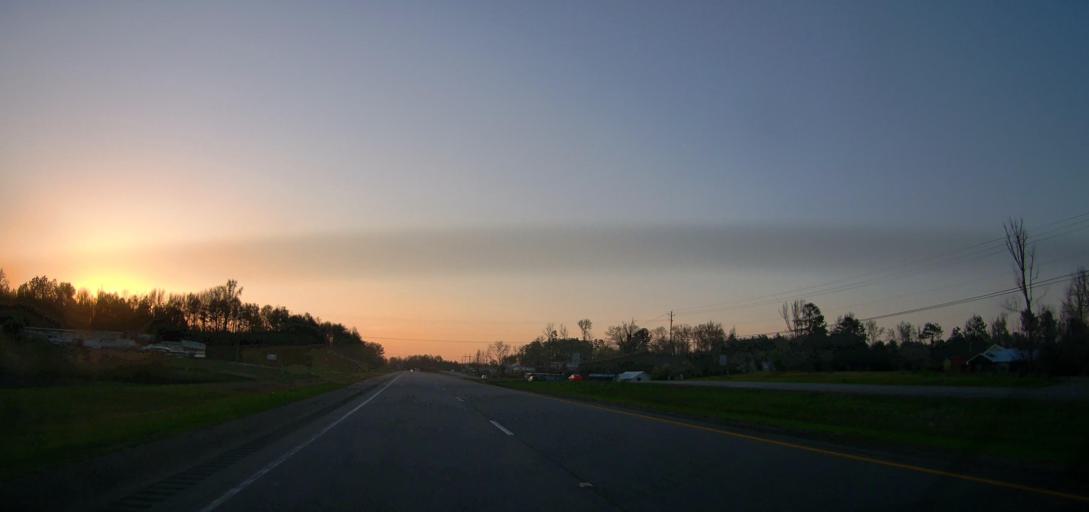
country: US
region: Alabama
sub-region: Tallapoosa County
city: Alexander City
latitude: 32.9688
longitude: -86.0118
